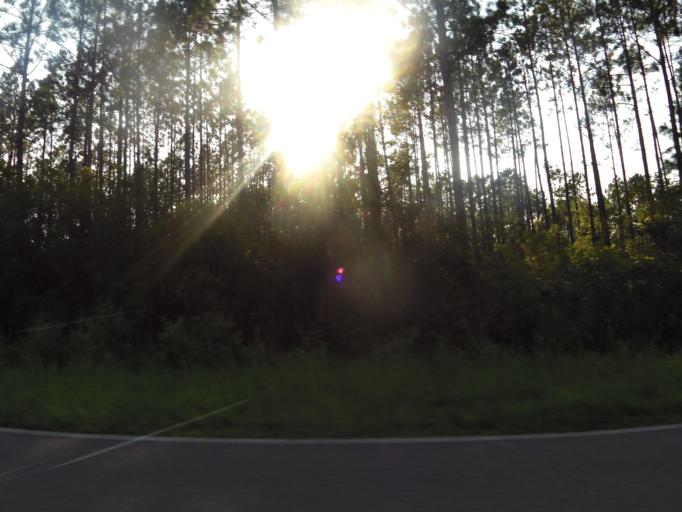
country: US
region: Florida
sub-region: Duval County
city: Baldwin
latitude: 30.3468
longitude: -82.0092
